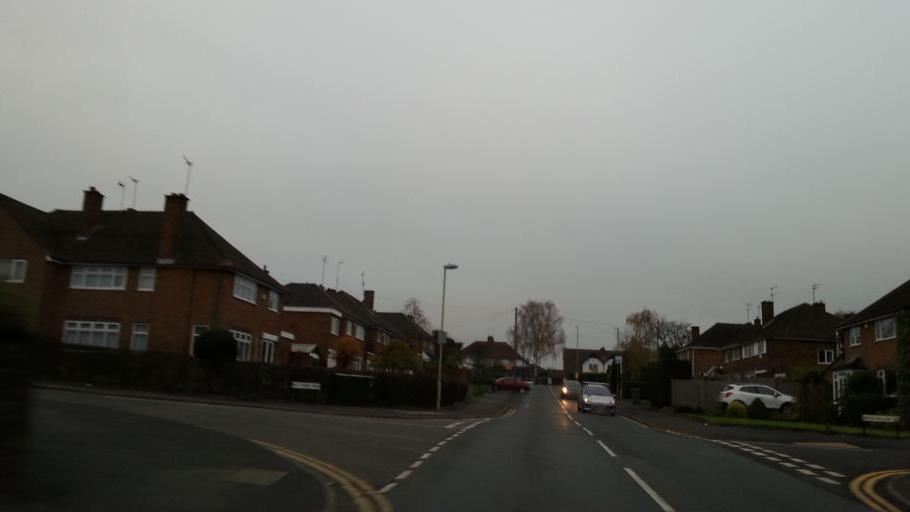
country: GB
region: England
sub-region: Dudley
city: Halesowen
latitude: 52.4407
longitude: -2.0732
